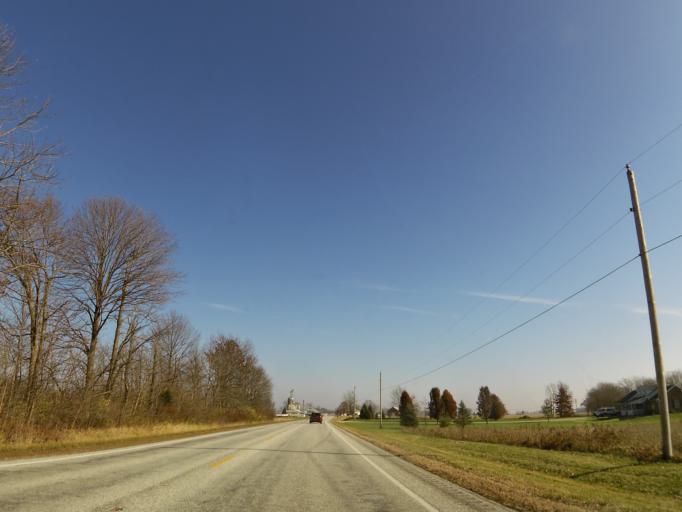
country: US
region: Indiana
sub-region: Shelby County
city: Shelbyville
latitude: 39.5523
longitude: -85.6749
